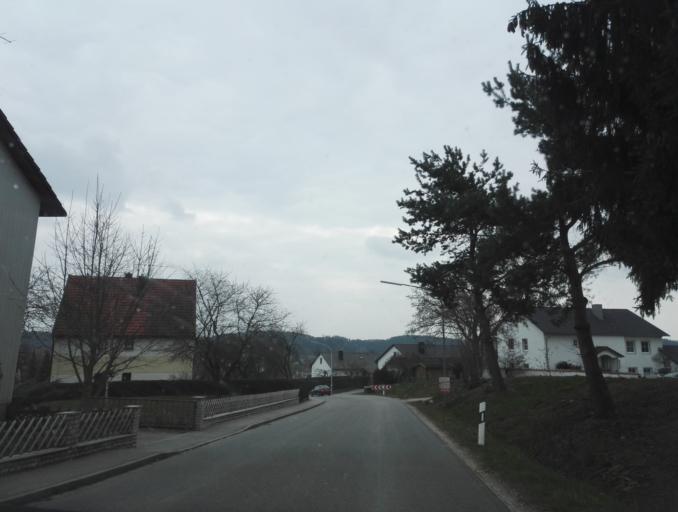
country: DE
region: Bavaria
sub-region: Lower Bavaria
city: Rottenburg an der Laaber
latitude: 48.6660
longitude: 12.0285
